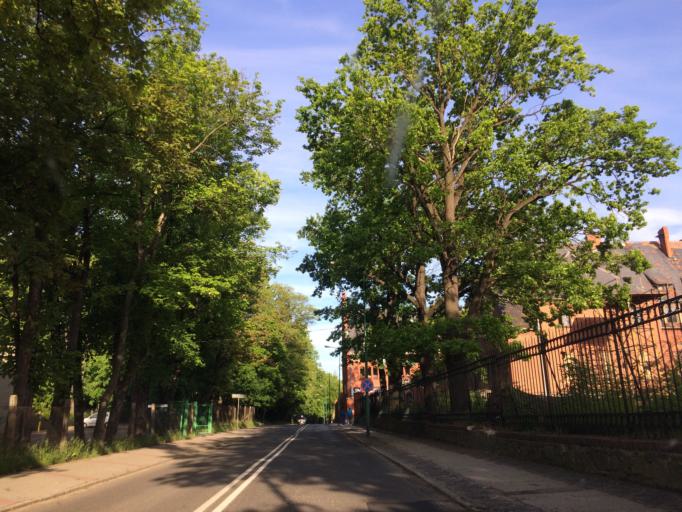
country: PL
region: Lower Silesian Voivodeship
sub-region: Powiat swidnicki
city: Swidnica
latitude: 50.8405
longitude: 16.4730
